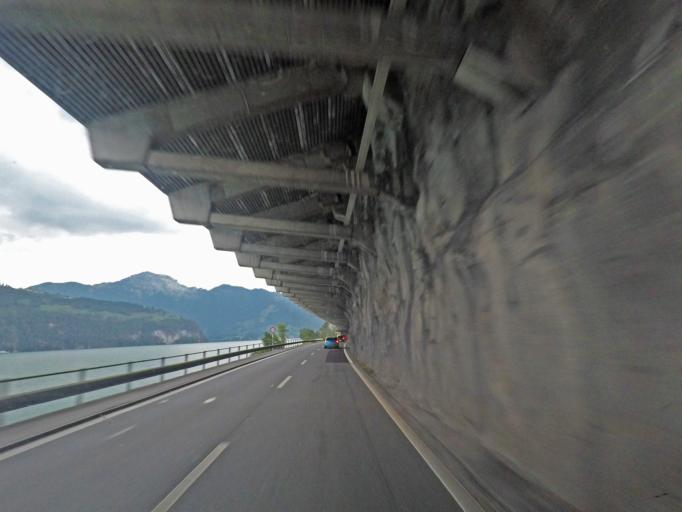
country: CH
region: Schwyz
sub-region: Bezirk Schwyz
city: Ingenbohl
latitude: 46.9624
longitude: 8.6162
